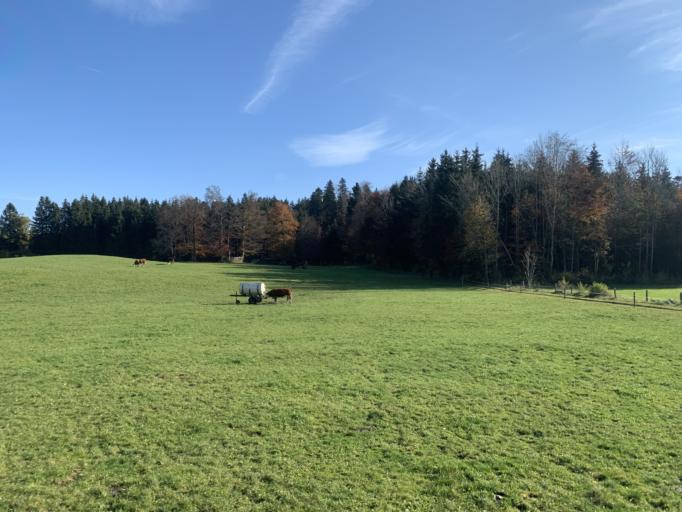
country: DE
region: Bavaria
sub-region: Upper Bavaria
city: Waakirchen
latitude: 47.7857
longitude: 11.7012
